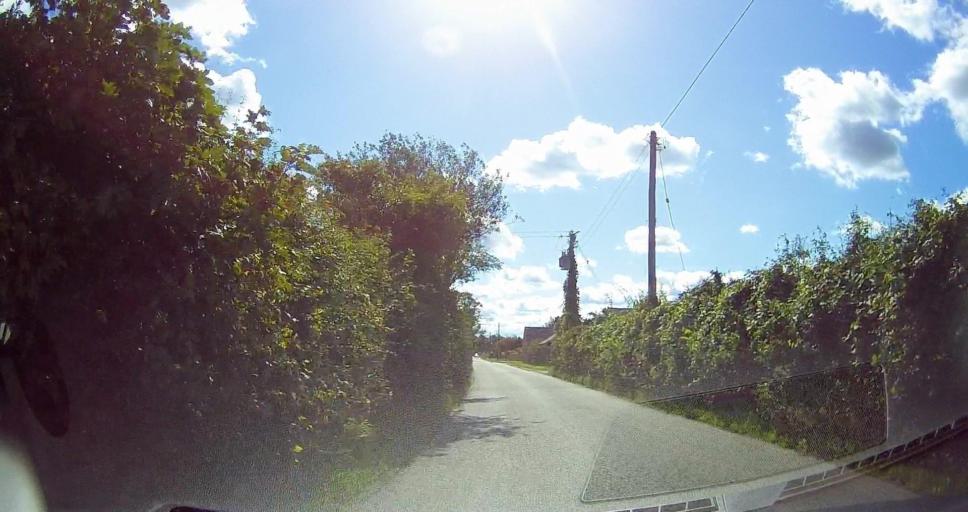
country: GB
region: England
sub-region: Cheshire East
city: Nantwich
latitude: 52.9962
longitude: -2.5340
